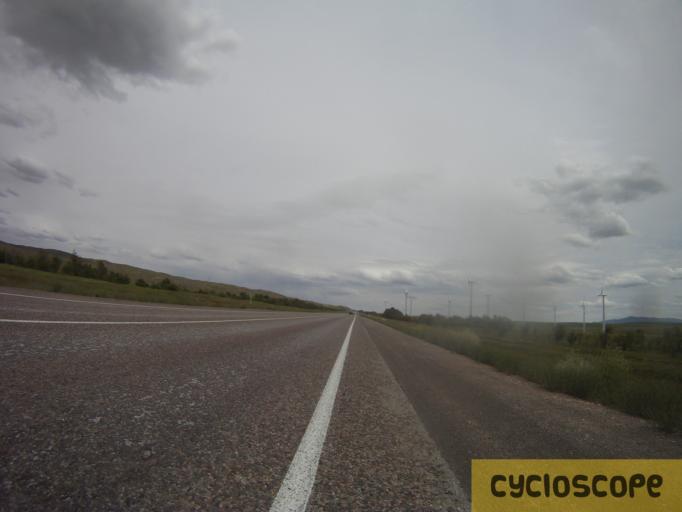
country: KZ
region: Zhambyl
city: Georgiyevka
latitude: 43.3347
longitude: 74.9563
